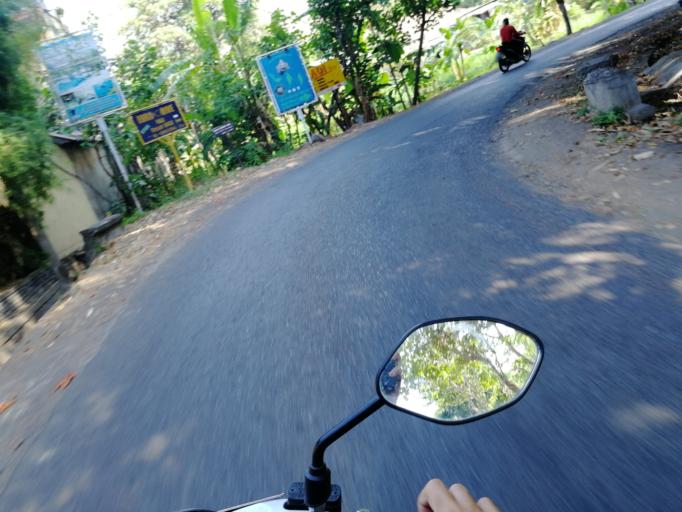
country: ID
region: Bali
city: Biaslantang Kaler
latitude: -8.3432
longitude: 115.6691
